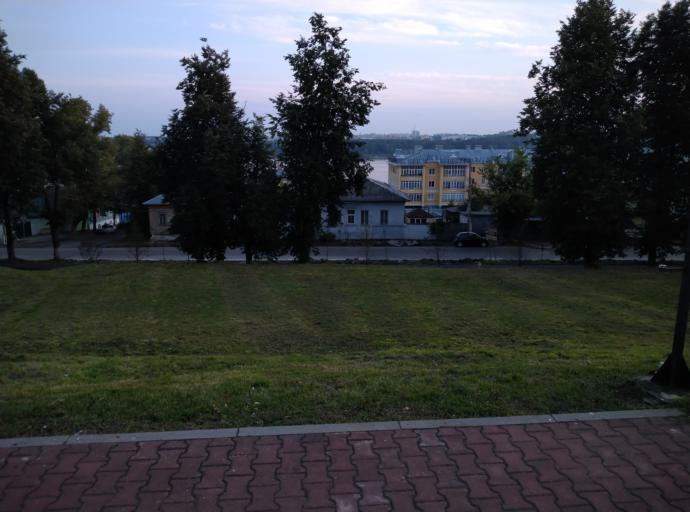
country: RU
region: Kostroma
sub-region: Kostromskoy Rayon
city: Kostroma
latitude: 57.7597
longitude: 40.9402
